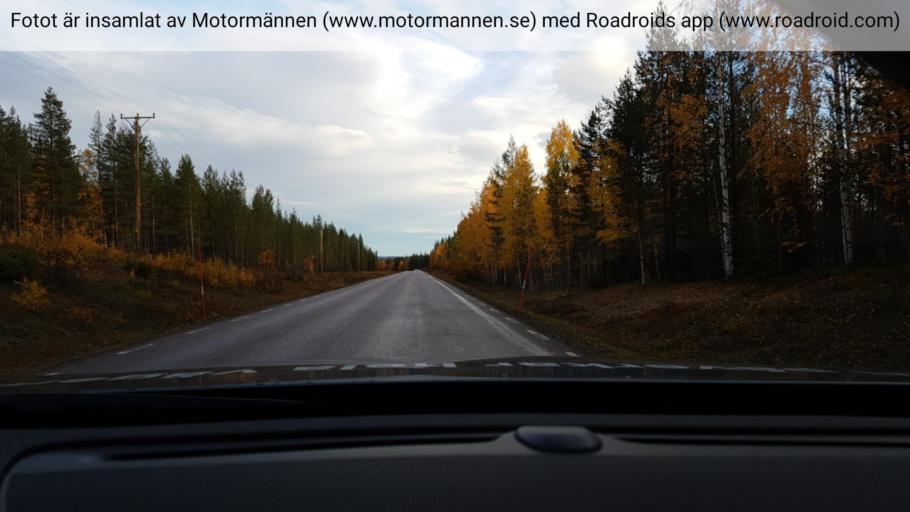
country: SE
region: Norrbotten
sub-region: Overkalix Kommun
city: OEverkalix
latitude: 67.0180
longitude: 22.5235
